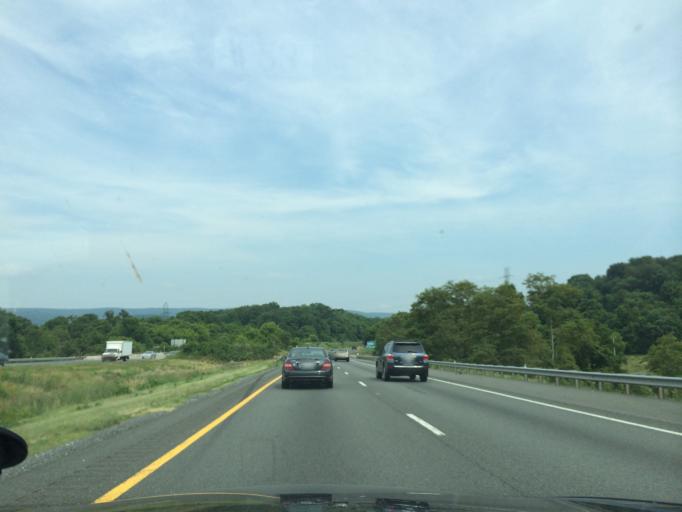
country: US
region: Maryland
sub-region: Frederick County
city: Myersville
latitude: 39.5070
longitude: -77.5868
